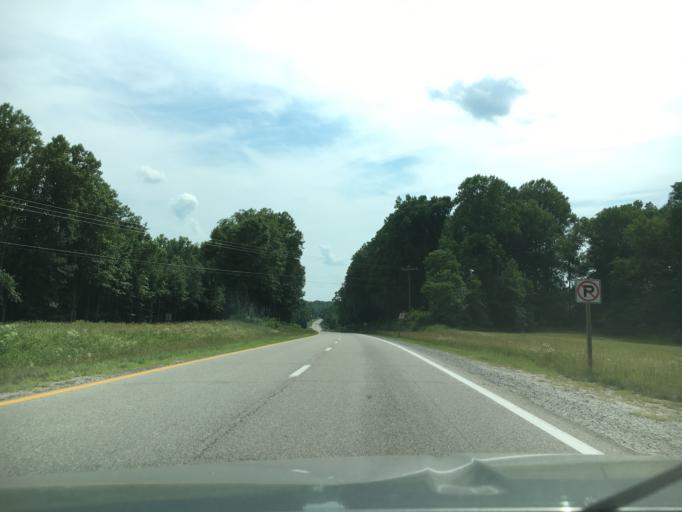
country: US
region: Virginia
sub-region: Lunenburg County
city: Victoria
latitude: 37.1305
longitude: -78.3198
